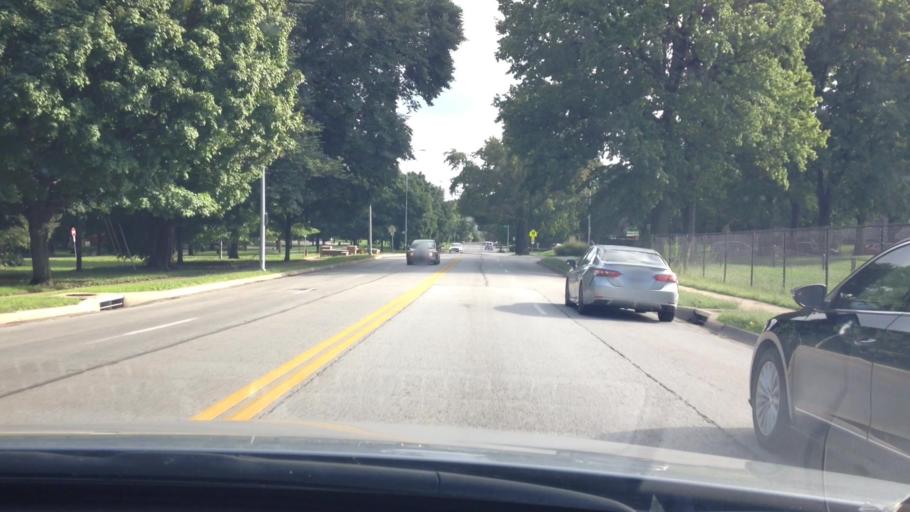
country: US
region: Kansas
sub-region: Johnson County
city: Mission Hills
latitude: 39.0090
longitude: -94.5933
